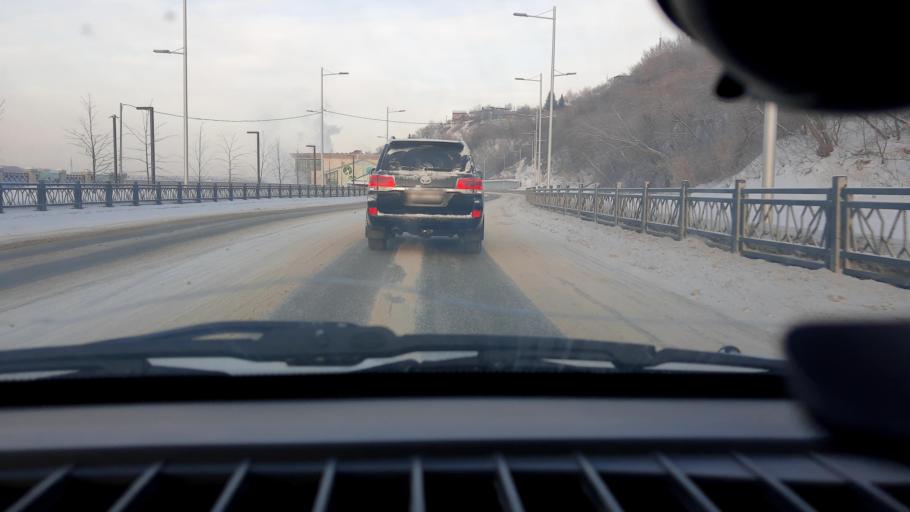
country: RU
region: Bashkortostan
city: Ufa
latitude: 54.7125
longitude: 55.9408
